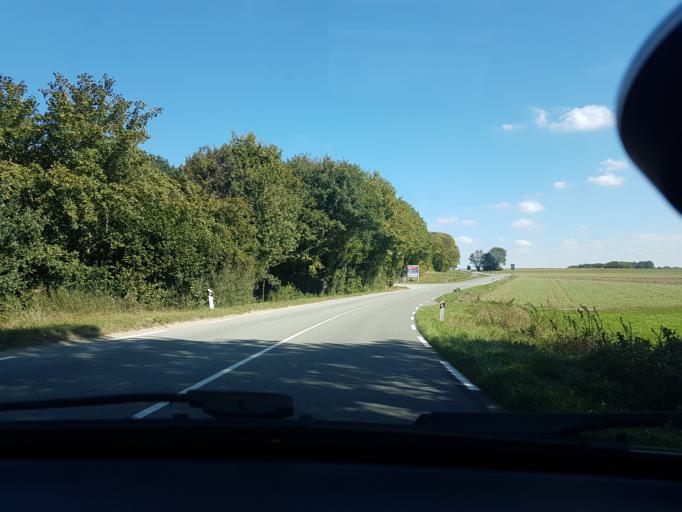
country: FR
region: Franche-Comte
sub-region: Territoire de Belfort
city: Chevremont
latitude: 47.6385
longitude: 6.9013
